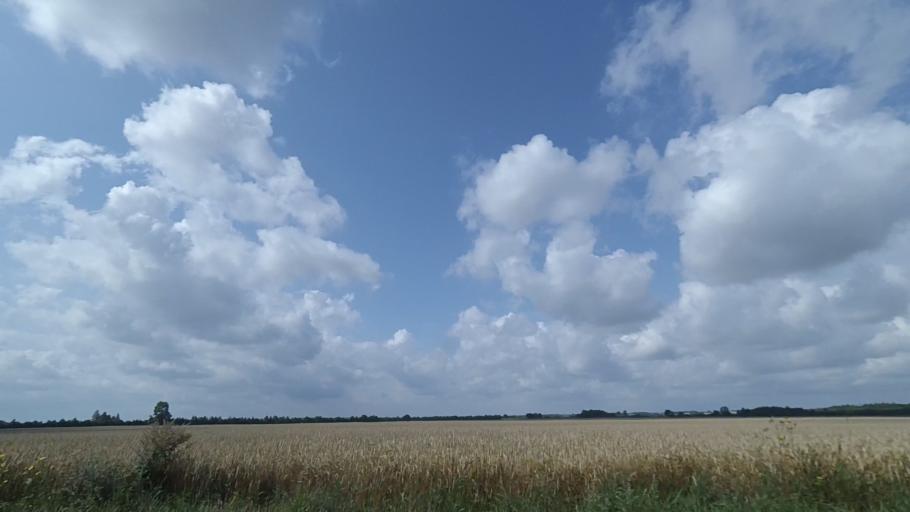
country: DK
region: Central Jutland
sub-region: Norddjurs Kommune
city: Auning
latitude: 56.5074
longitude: 10.4215
